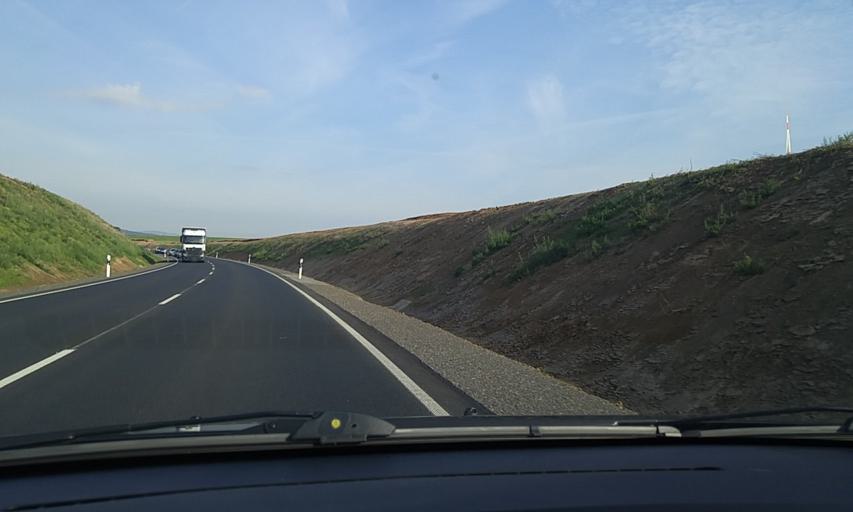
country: DE
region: Hesse
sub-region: Regierungsbezirk Darmstadt
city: Friedberg
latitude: 50.2995
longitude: 8.7660
